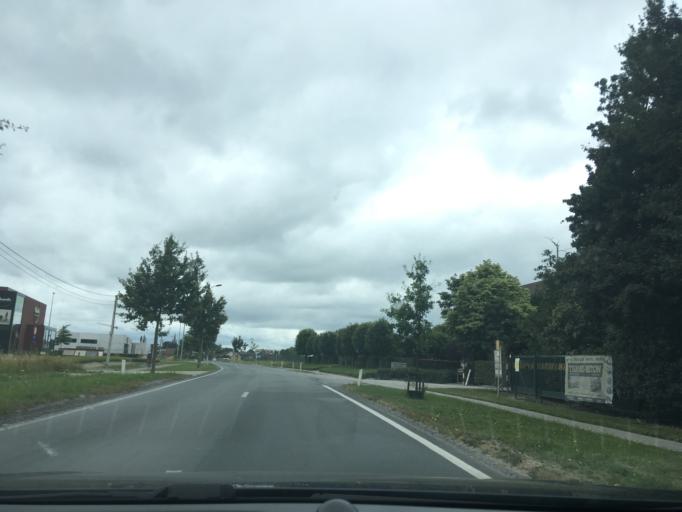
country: BE
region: Flanders
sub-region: Provincie West-Vlaanderen
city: Wingene
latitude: 51.0519
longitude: 3.2908
